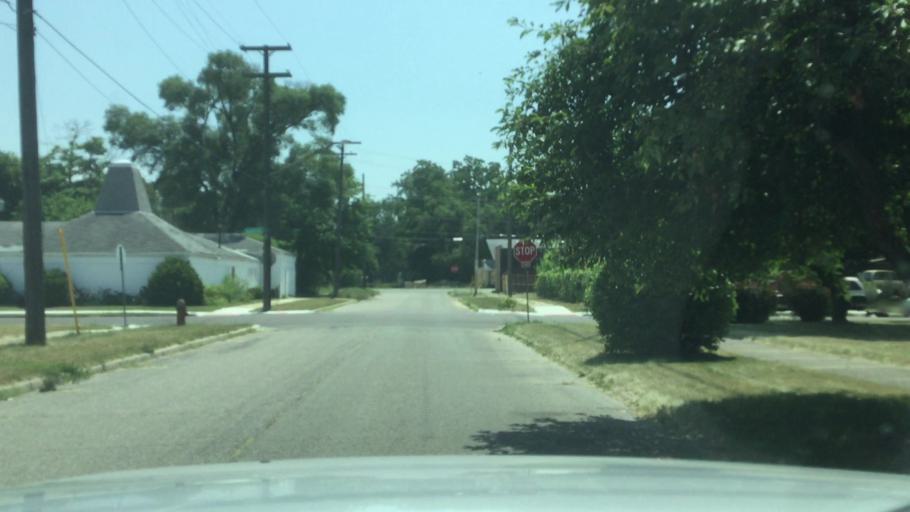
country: US
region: Michigan
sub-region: Wayne County
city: Detroit
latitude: 42.3551
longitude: -83.0207
